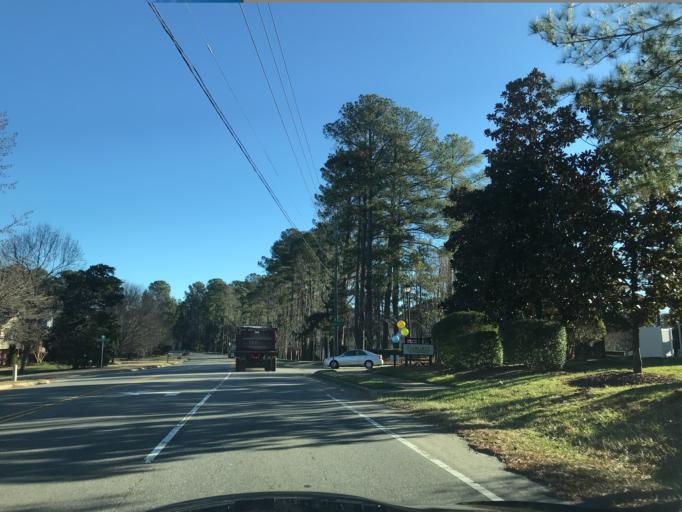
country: US
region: North Carolina
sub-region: Wake County
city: Cary
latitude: 35.9016
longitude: -78.7299
